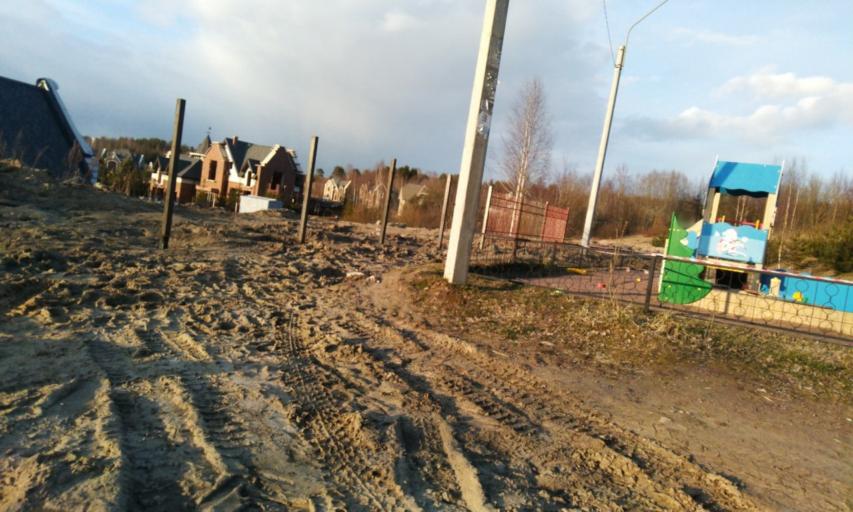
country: RU
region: Leningrad
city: Novoye Devyatkino
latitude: 60.1075
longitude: 30.4542
